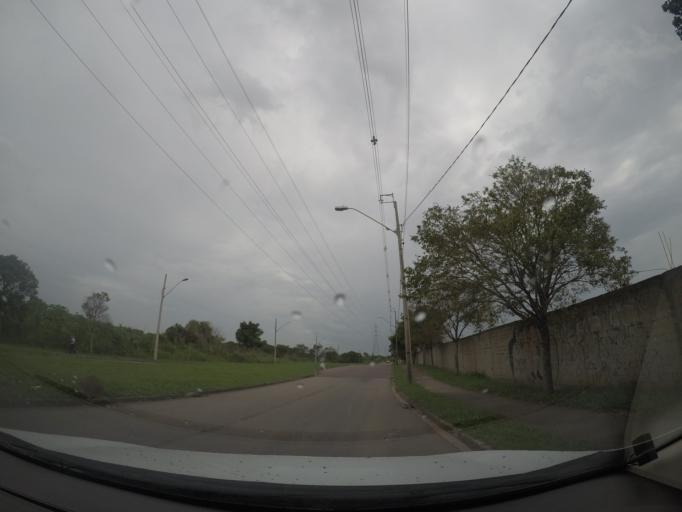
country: BR
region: Parana
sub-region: Sao Jose Dos Pinhais
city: Sao Jose dos Pinhais
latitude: -25.5051
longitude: -49.2131
